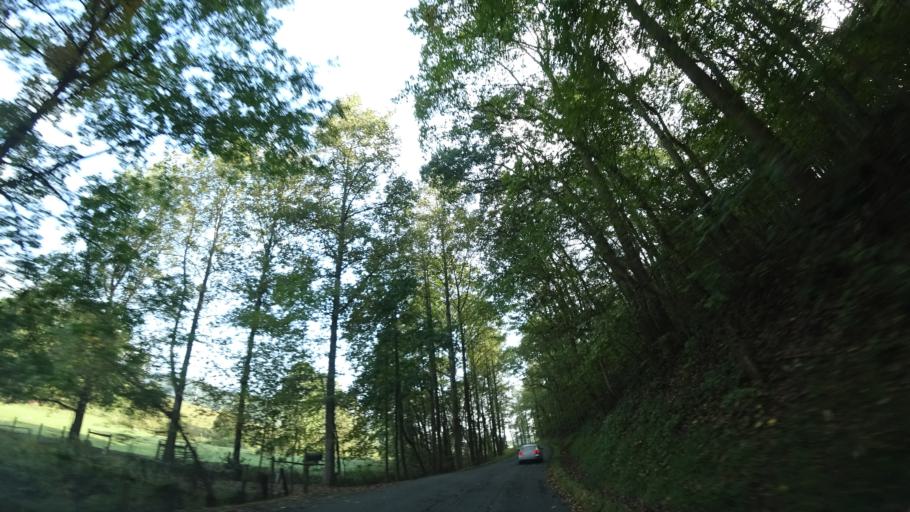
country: US
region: Virginia
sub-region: Madison County
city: Madison
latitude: 38.5102
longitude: -78.3094
